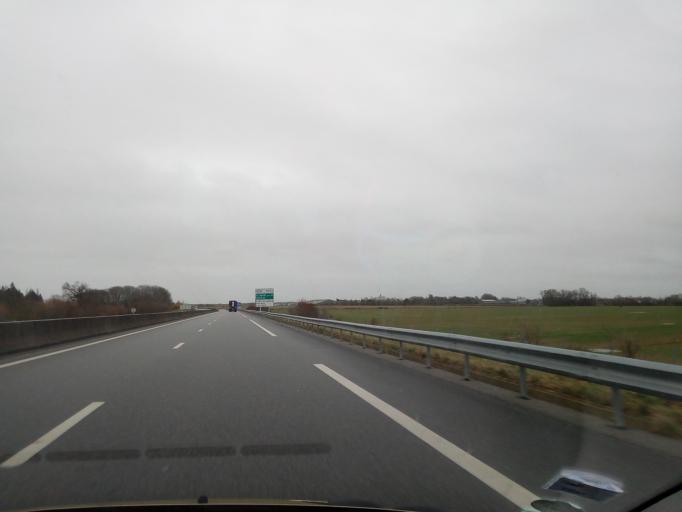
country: FR
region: Haute-Normandie
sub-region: Departement de l'Eure
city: Bernay
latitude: 49.1400
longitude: 0.5600
